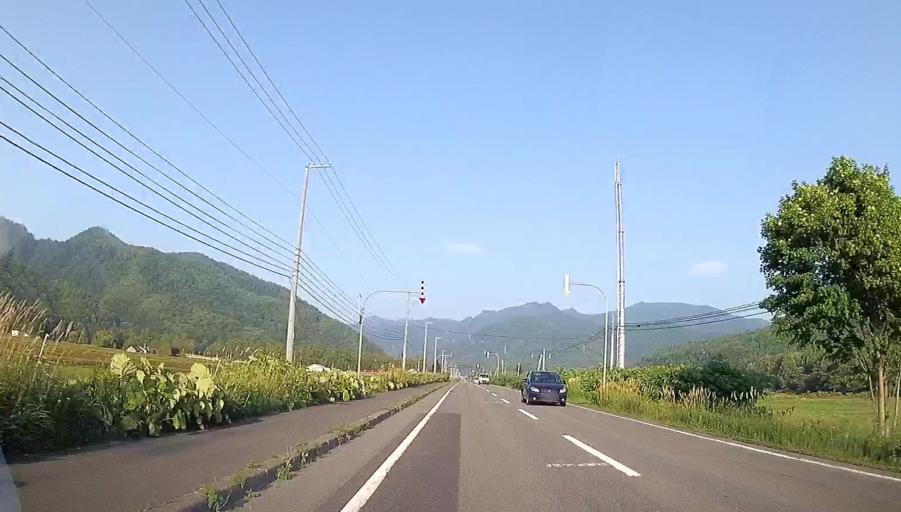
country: JP
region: Hokkaido
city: Shimo-furano
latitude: 42.8935
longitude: 142.5153
